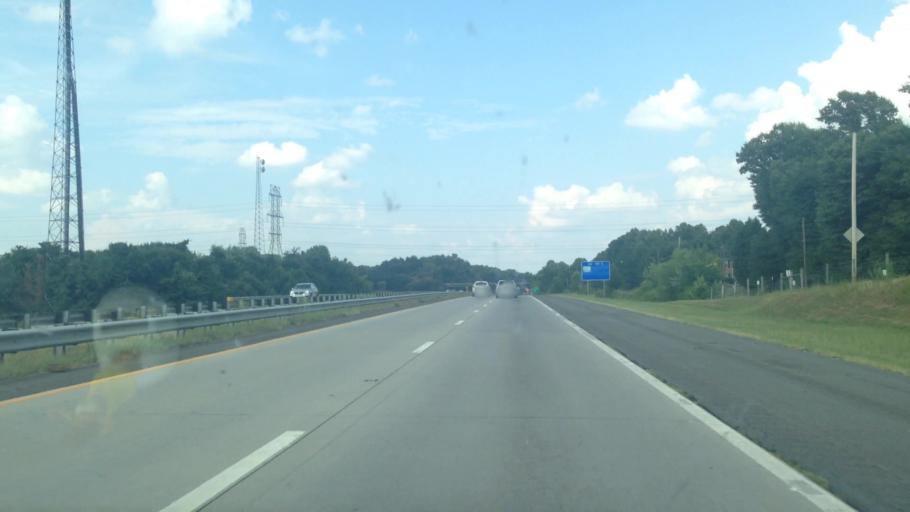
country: US
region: North Carolina
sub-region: Forsyth County
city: Walkertown
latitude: 36.1084
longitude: -80.1709
